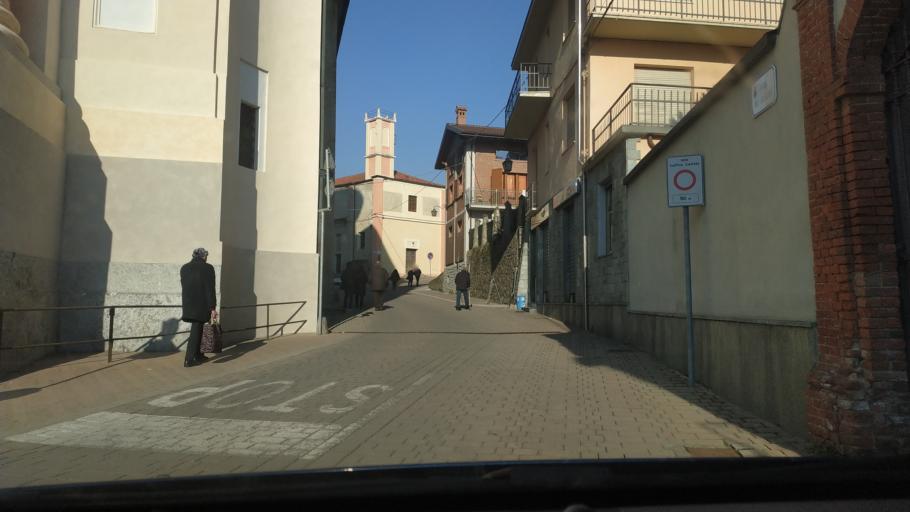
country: IT
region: Piedmont
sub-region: Provincia di Torino
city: Pavone Canavese
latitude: 45.4355
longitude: 7.8543
